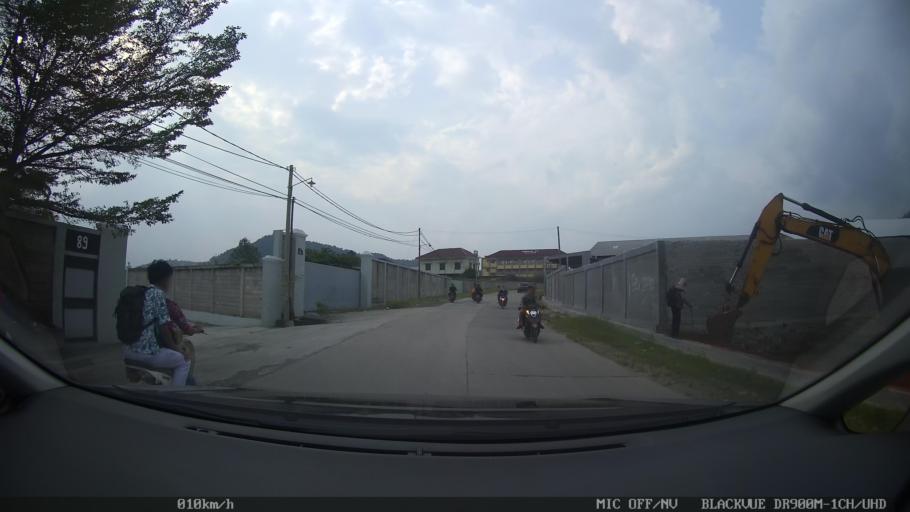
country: ID
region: Lampung
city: Bandarlampung
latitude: -5.4378
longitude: 105.2965
